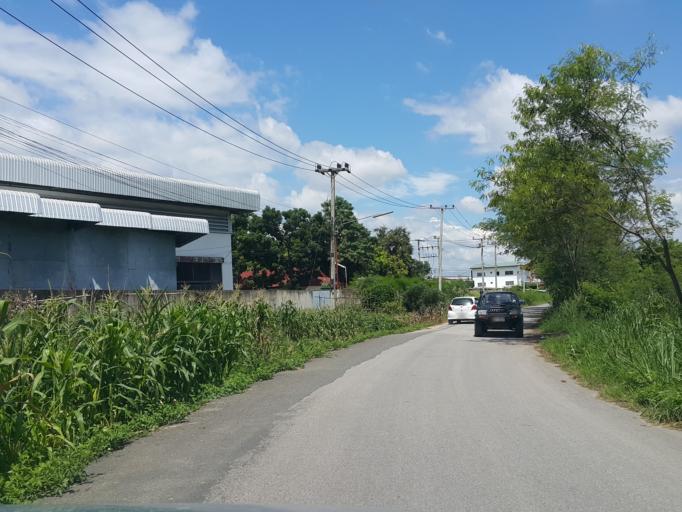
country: TH
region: Chiang Mai
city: Chiang Mai
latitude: 18.7404
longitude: 98.9606
